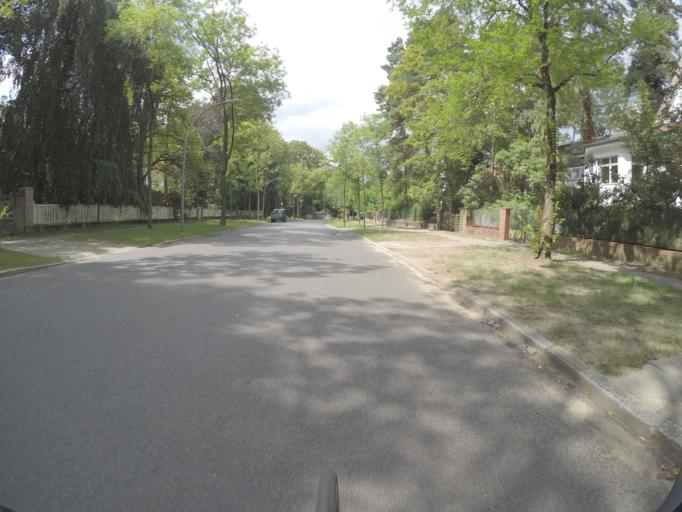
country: DE
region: Berlin
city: Frohnau
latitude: 52.6320
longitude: 13.2958
